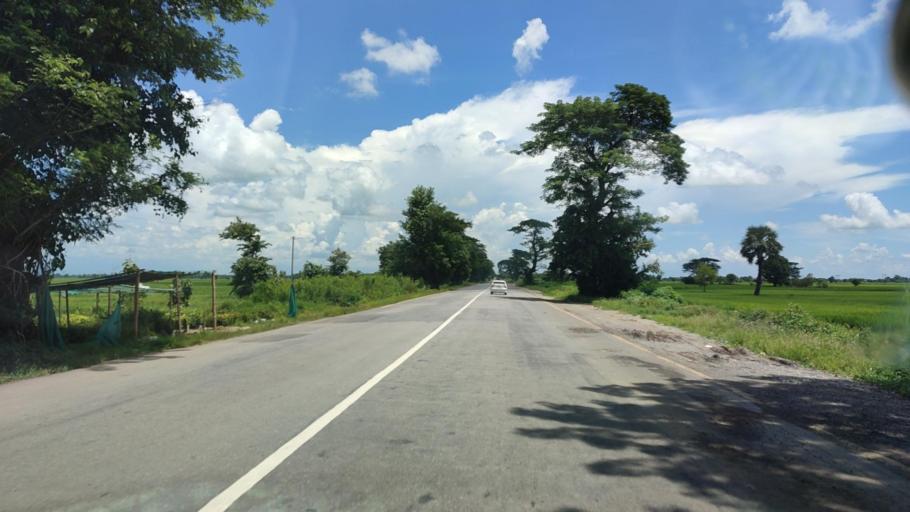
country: MM
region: Bago
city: Nyaunglebin
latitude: 18.1978
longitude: 96.5650
